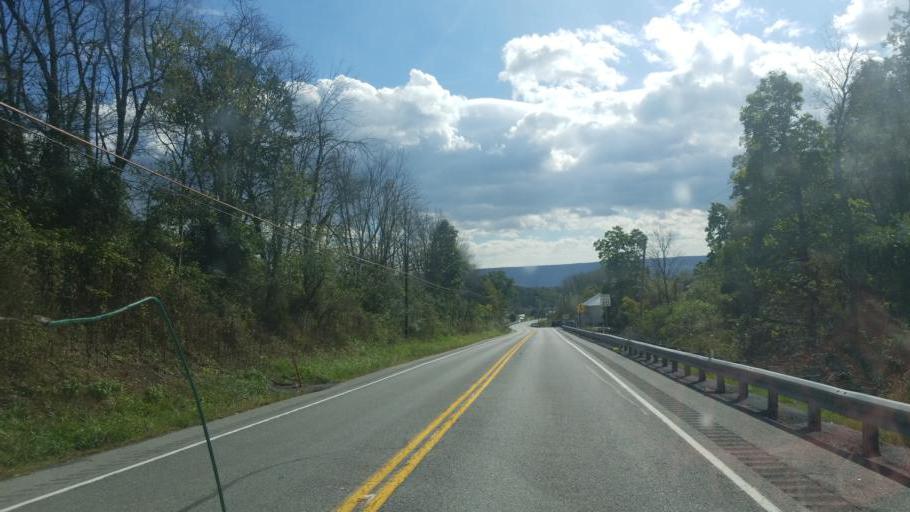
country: US
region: Pennsylvania
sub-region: Fulton County
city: McConnellsburg
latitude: 40.0087
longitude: -78.1073
